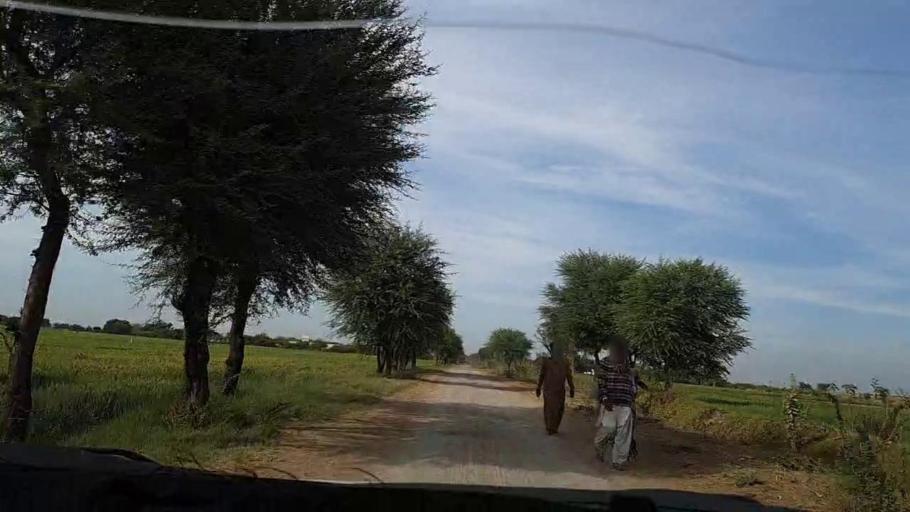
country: PK
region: Sindh
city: Dhoro Naro
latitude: 25.4454
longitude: 69.5124
